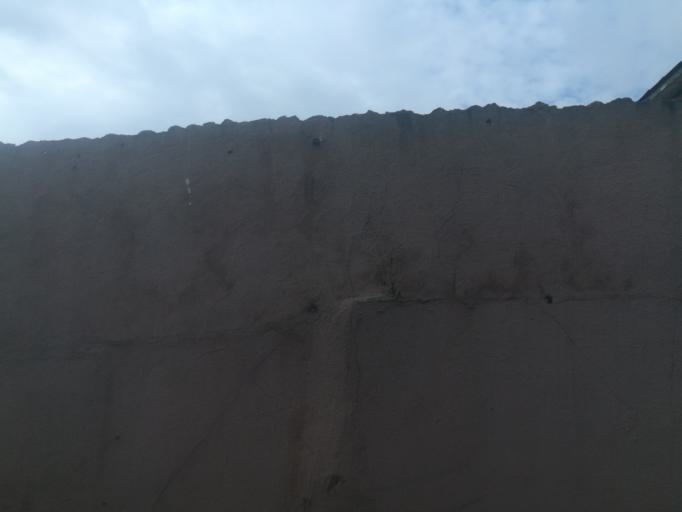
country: NG
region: Lagos
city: Somolu
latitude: 6.5494
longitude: 3.3709
